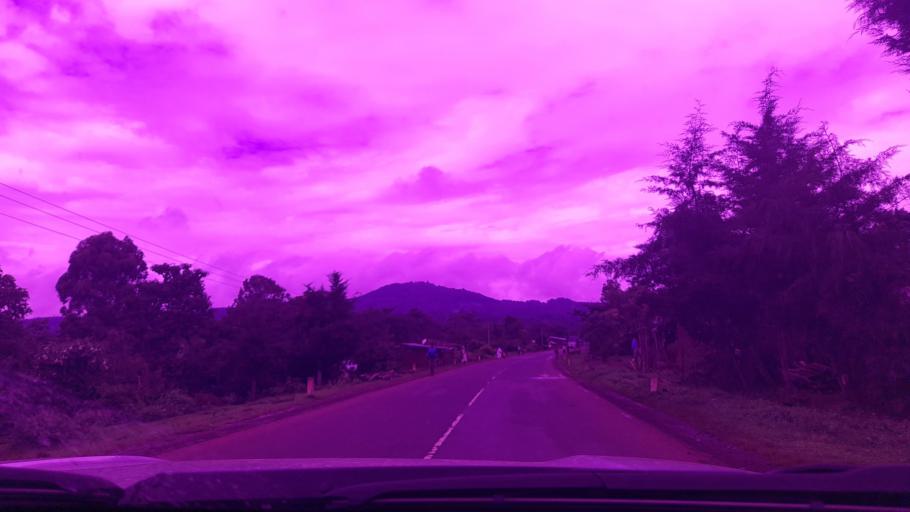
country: ET
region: Oromiya
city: Jima
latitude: 7.5553
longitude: 36.6184
